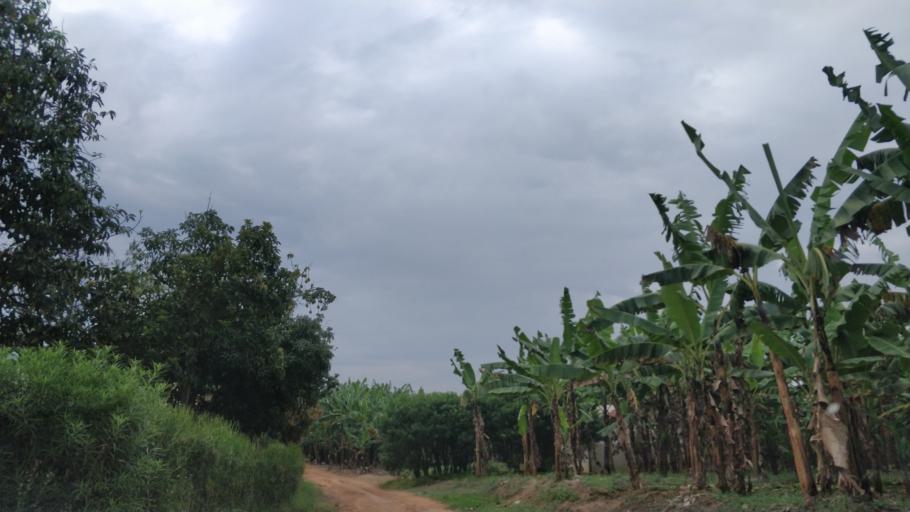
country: UG
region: Western Region
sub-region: Sheema District
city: Kibingo
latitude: -0.6411
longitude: 30.4909
